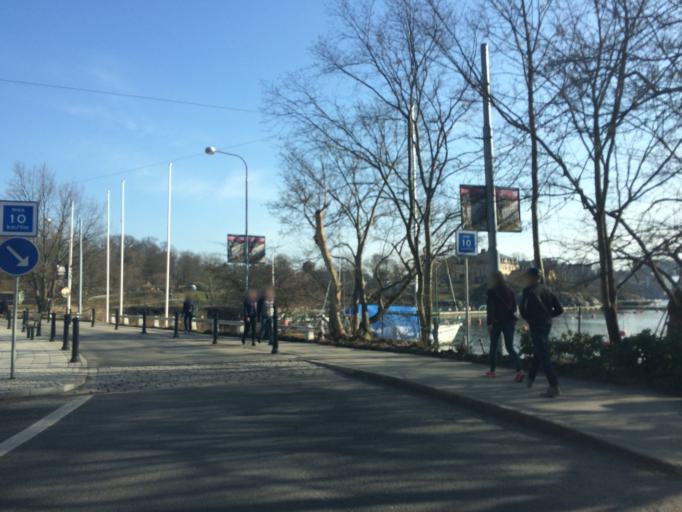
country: SE
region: Stockholm
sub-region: Stockholms Kommun
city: OEstermalm
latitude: 59.3227
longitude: 18.1106
